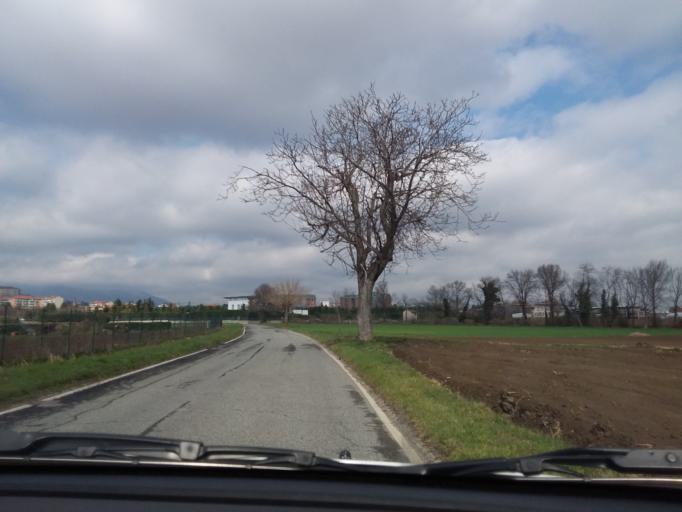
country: IT
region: Piedmont
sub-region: Provincia di Torino
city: Rivoli
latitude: 45.0579
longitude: 7.5279
